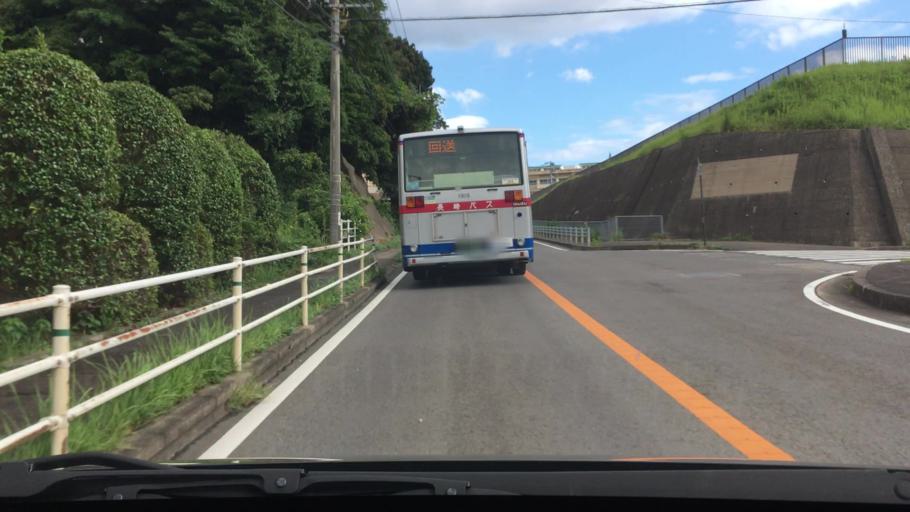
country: JP
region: Nagasaki
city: Togitsu
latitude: 32.8257
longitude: 129.7556
